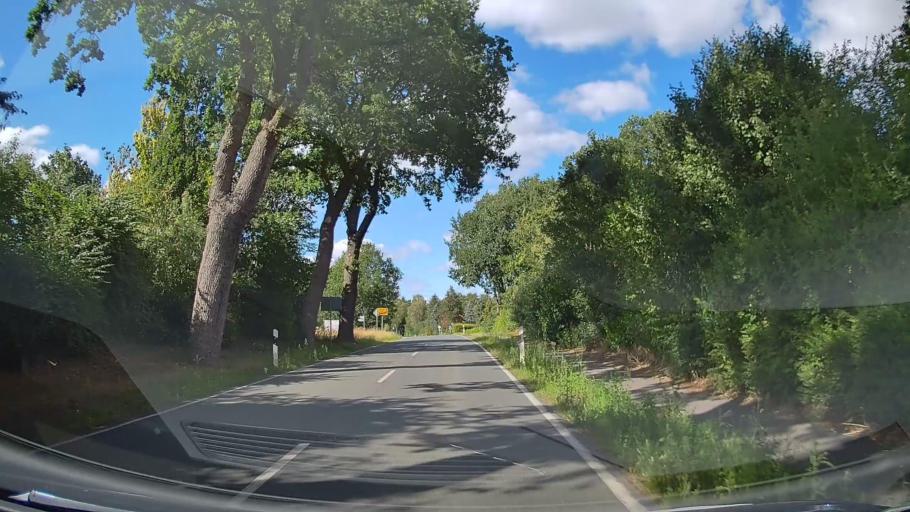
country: DE
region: Lower Saxony
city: Bippen
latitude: 52.5860
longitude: 7.7403
